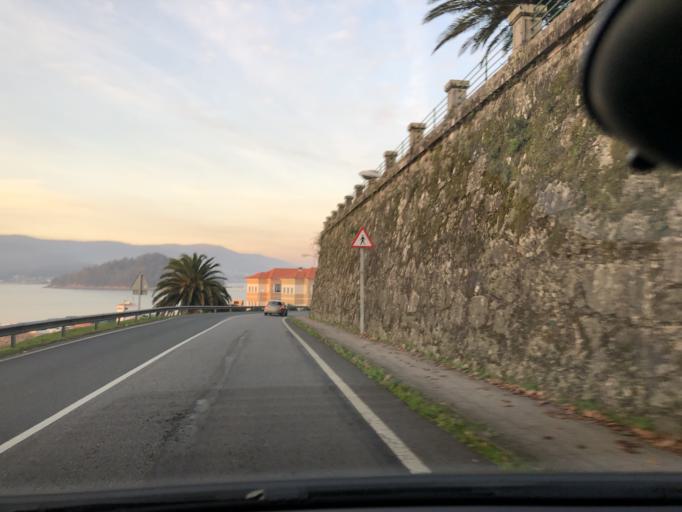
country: ES
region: Galicia
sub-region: Provincia de Pontevedra
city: Marin
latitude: 42.3930
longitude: -8.7099
